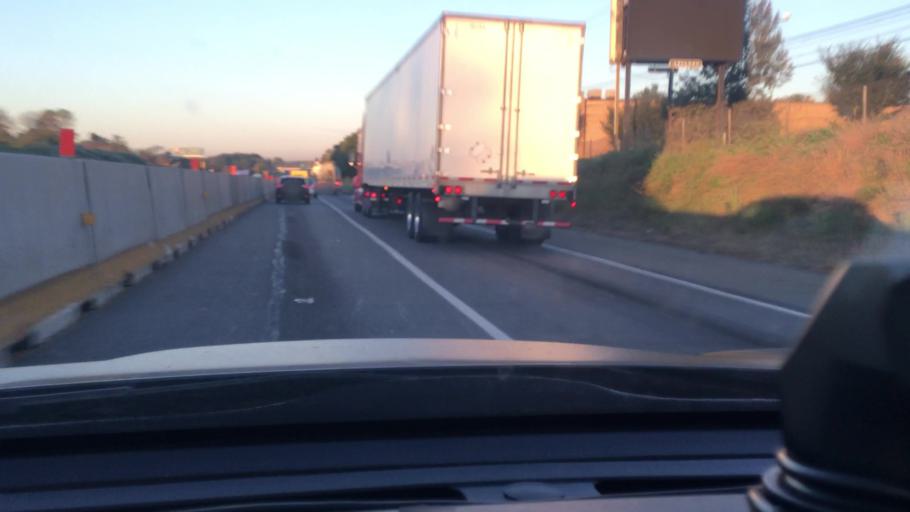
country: US
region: Pennsylvania
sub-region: Lehigh County
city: Fullerton
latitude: 40.6356
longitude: -75.4551
